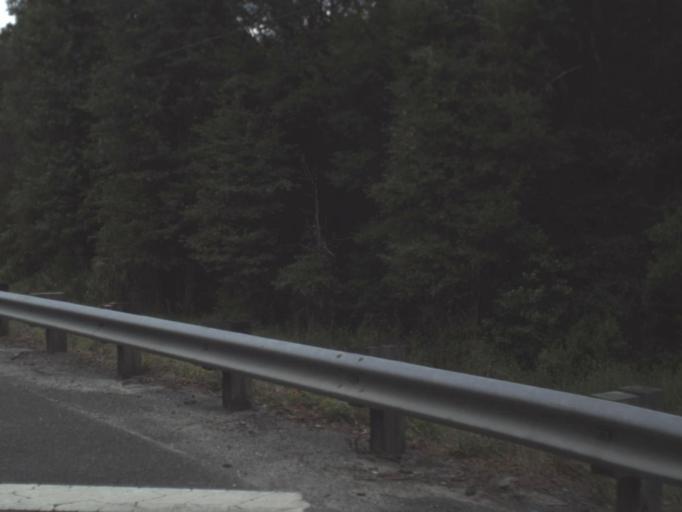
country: US
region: Florida
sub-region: Baker County
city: Macclenny
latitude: 30.3513
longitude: -82.1287
